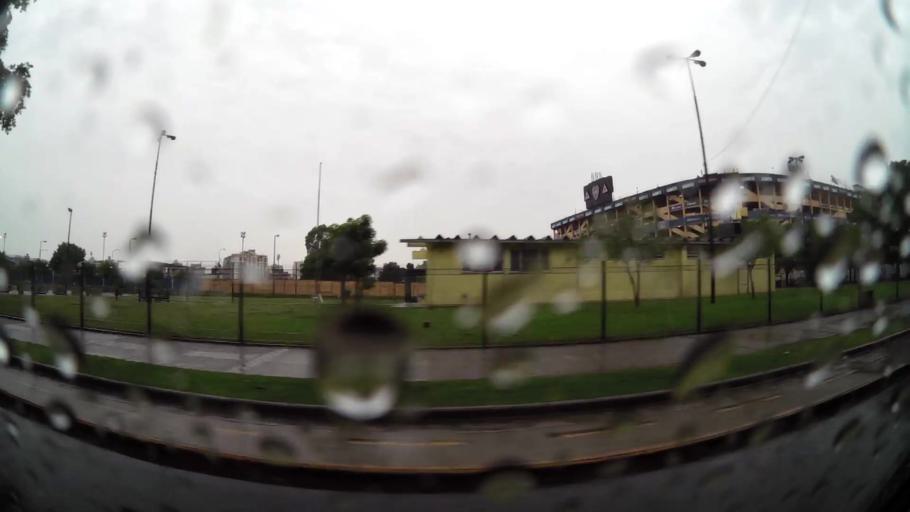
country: AR
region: Buenos Aires F.D.
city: Buenos Aires
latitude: -34.6347
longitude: -58.3670
